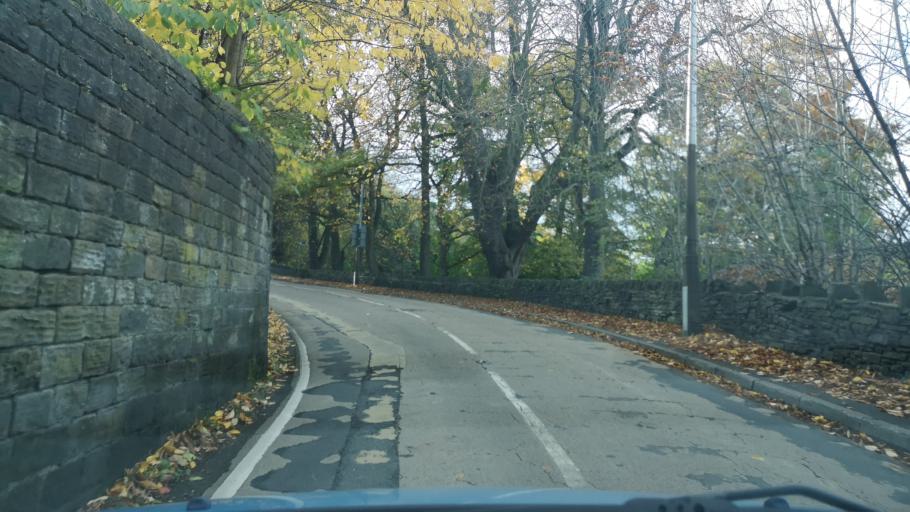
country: GB
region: England
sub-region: Kirklees
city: Mirfield
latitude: 53.6664
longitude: -1.7033
